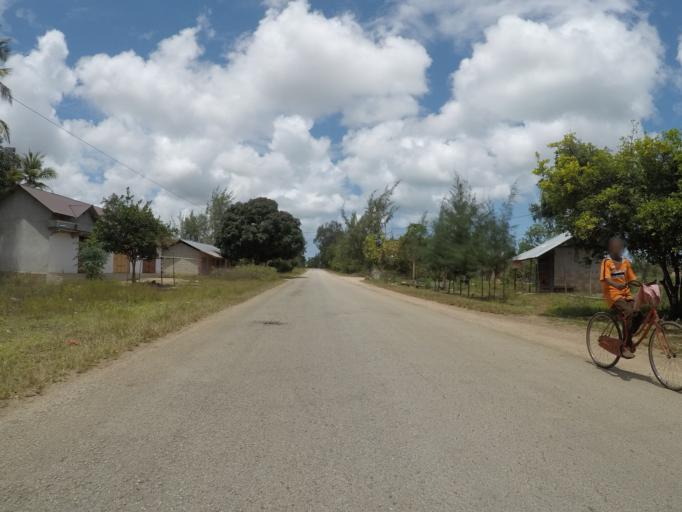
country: TZ
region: Zanzibar Central/South
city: Mahonda
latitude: -6.3106
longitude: 39.4320
